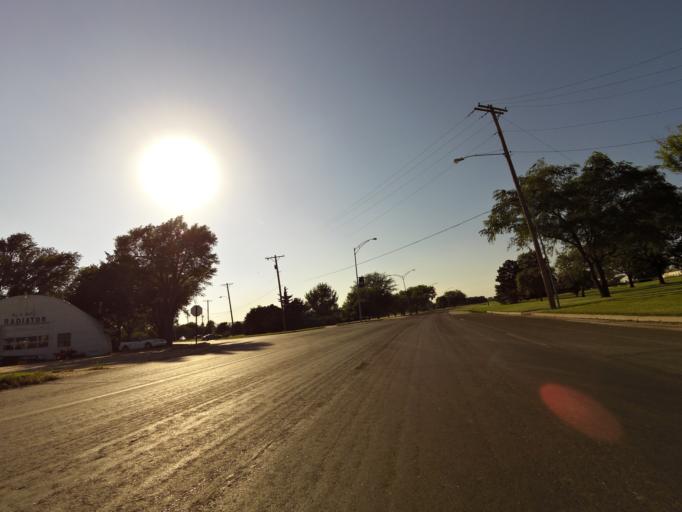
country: US
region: Kansas
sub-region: Harvey County
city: Hesston
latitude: 38.1394
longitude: -97.4331
